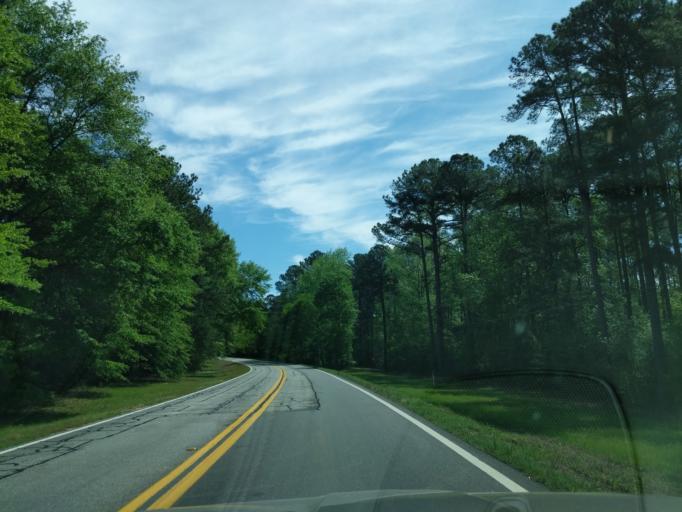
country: US
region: Georgia
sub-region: Columbia County
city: Appling
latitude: 33.6118
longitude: -82.3047
